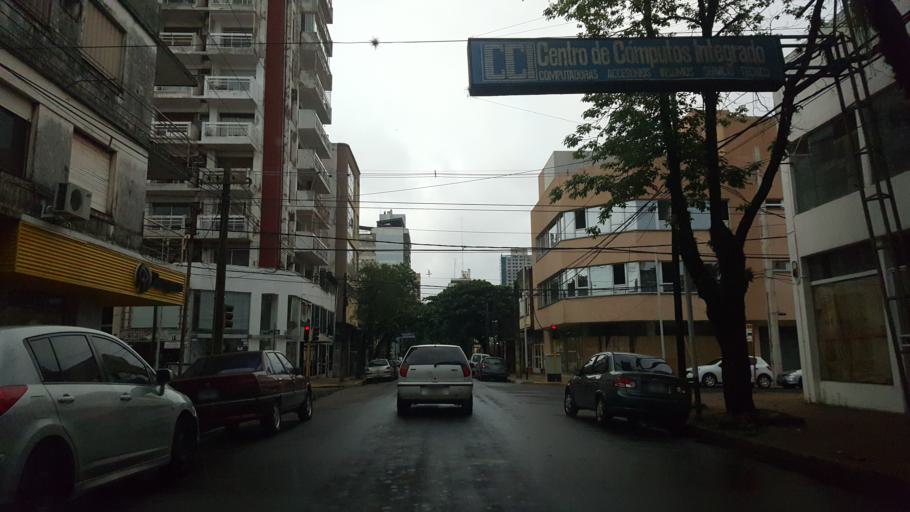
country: AR
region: Misiones
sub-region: Departamento de Capital
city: Posadas
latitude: -27.3728
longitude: -55.8955
